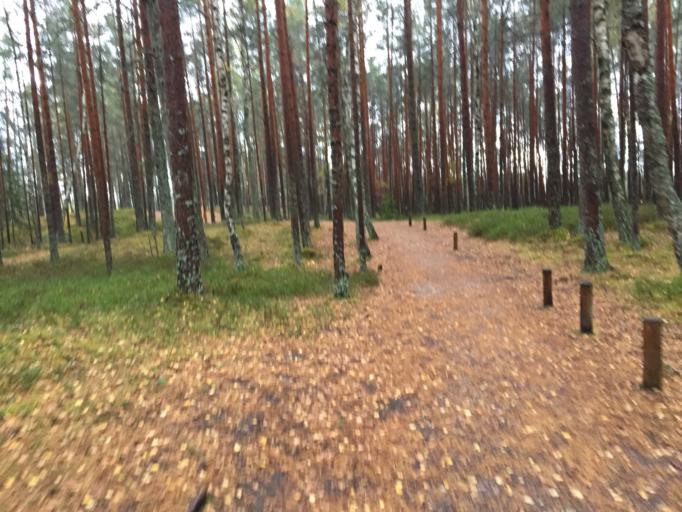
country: LV
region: Engure
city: Smarde
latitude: 56.9115
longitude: 23.4594
